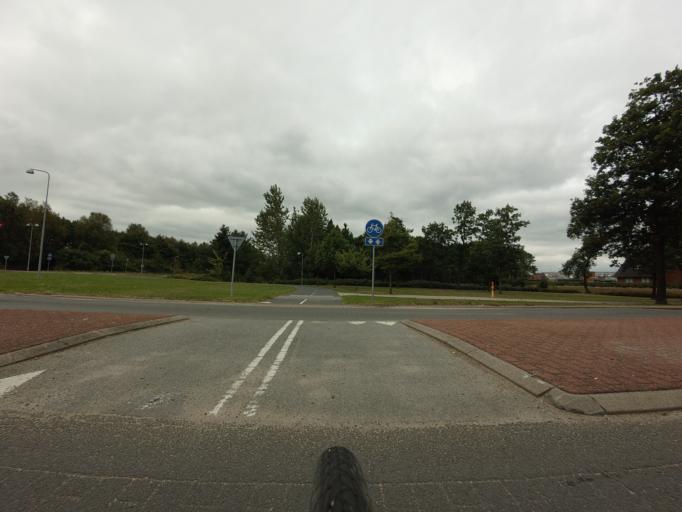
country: DK
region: South Denmark
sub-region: Billund Kommune
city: Grindsted
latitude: 55.7616
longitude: 8.9304
